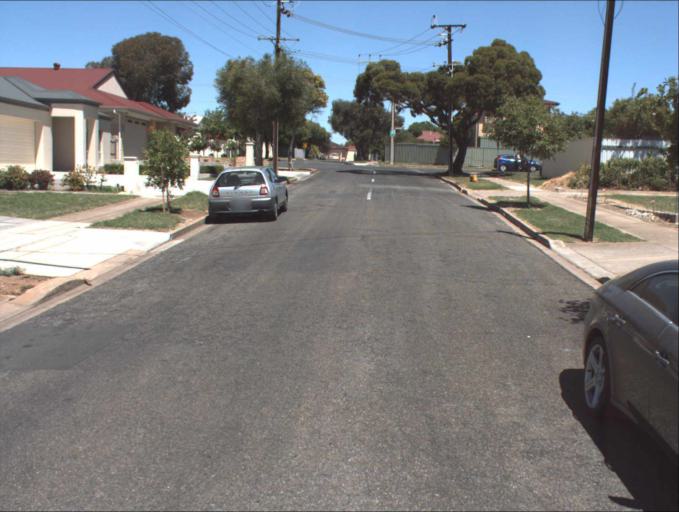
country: AU
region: South Australia
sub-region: Port Adelaide Enfield
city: Enfield
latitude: -34.8650
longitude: 138.6106
